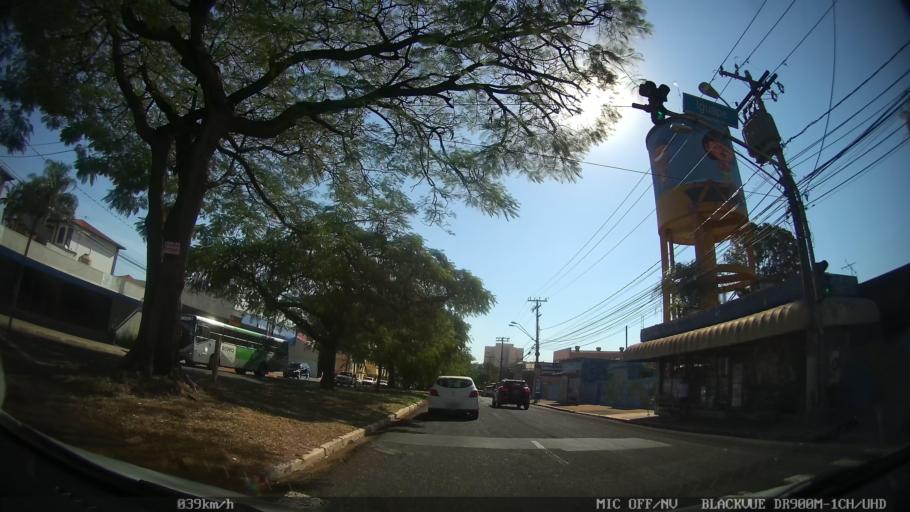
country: BR
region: Sao Paulo
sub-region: Ribeirao Preto
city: Ribeirao Preto
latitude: -21.1778
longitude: -47.7898
